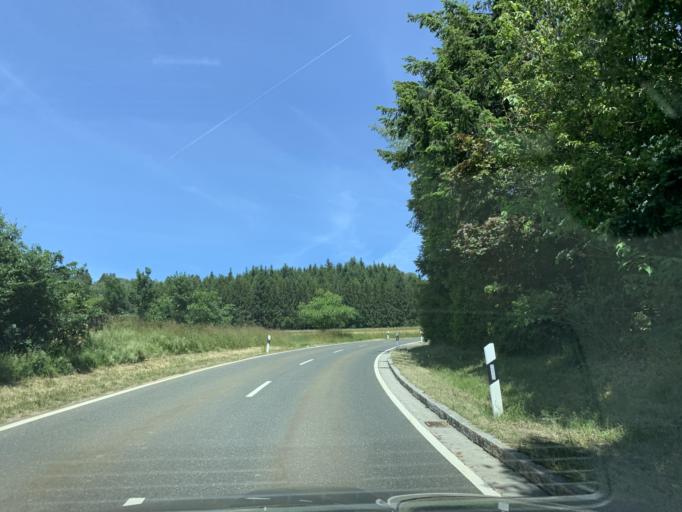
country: DE
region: Bavaria
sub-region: Upper Palatinate
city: Bach
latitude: 49.4098
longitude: 12.3624
